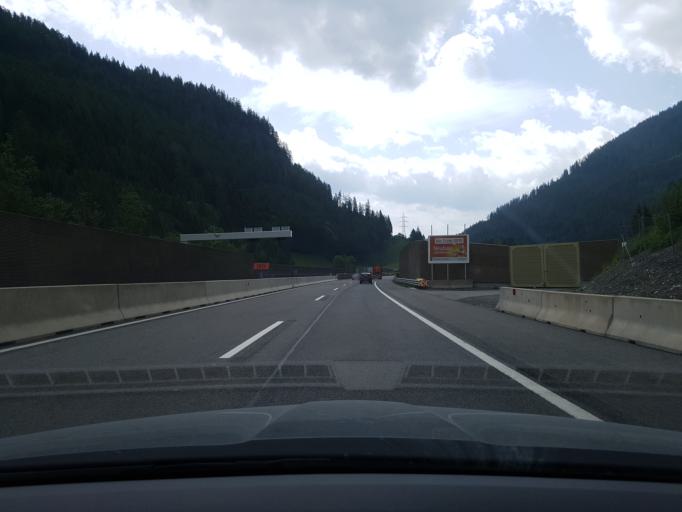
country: AT
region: Salzburg
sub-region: Politischer Bezirk Tamsweg
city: Zederhaus
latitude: 47.1464
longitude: 13.5176
